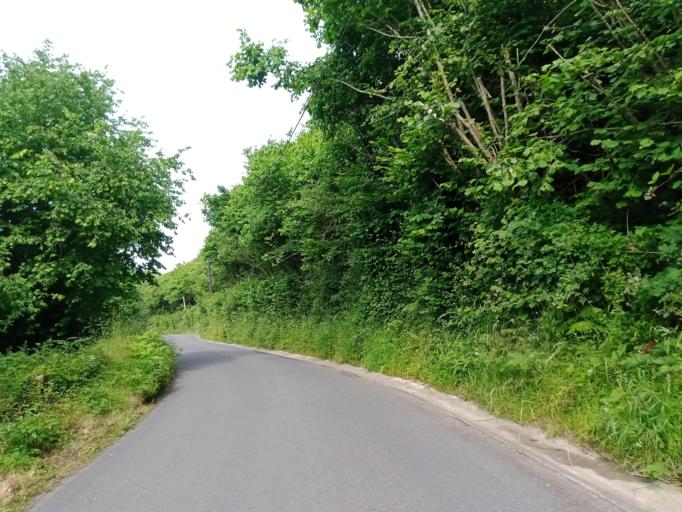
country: IE
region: Leinster
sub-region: Laois
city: Rathdowney
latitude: 52.8015
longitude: -7.4619
